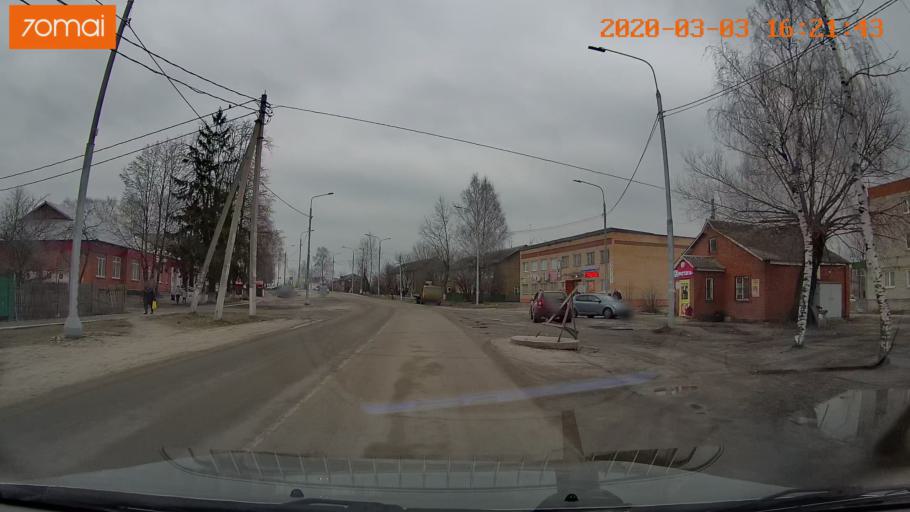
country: RU
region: Moskovskaya
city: Imeni Tsyurupy
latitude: 55.4965
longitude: 38.6458
